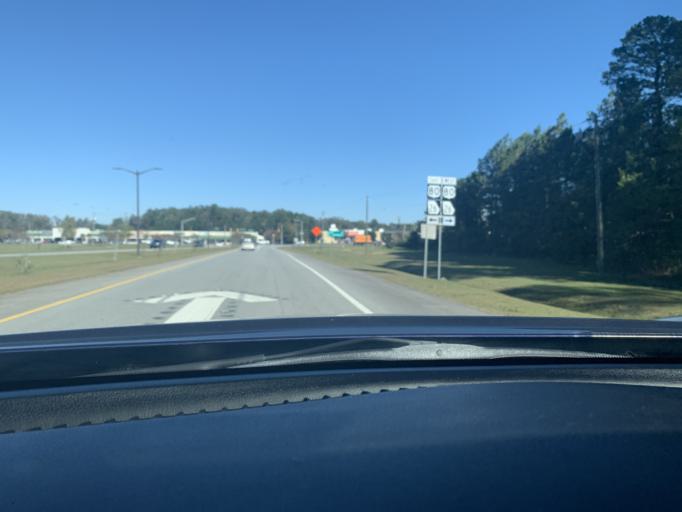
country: US
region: Georgia
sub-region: Chatham County
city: Pooler
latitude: 32.1199
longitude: -81.2662
